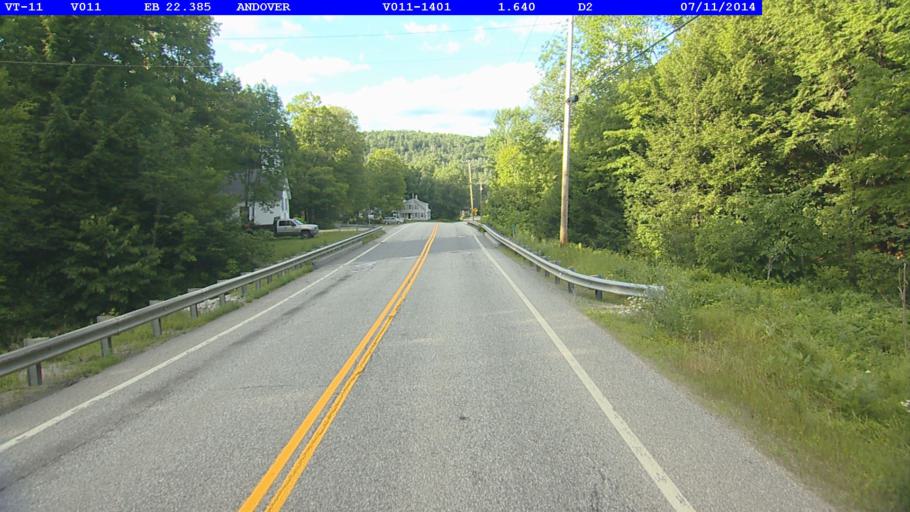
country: US
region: Vermont
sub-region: Windsor County
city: Chester
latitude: 43.2553
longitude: -72.7181
